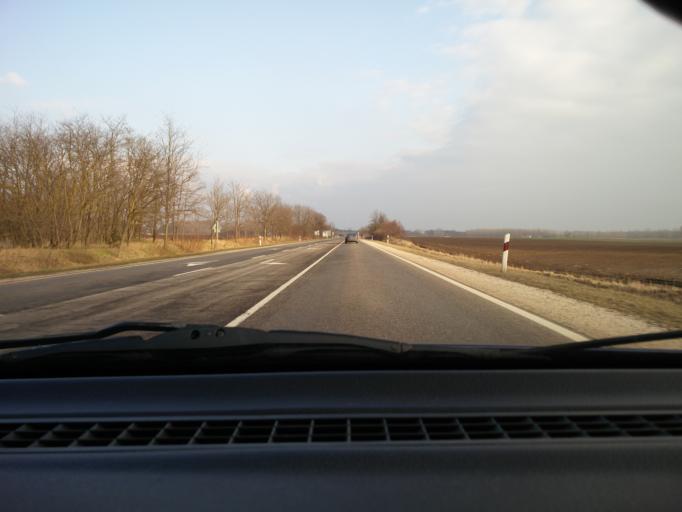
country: HU
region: Pest
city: Nyaregyhaza
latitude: 47.2472
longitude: 19.4823
